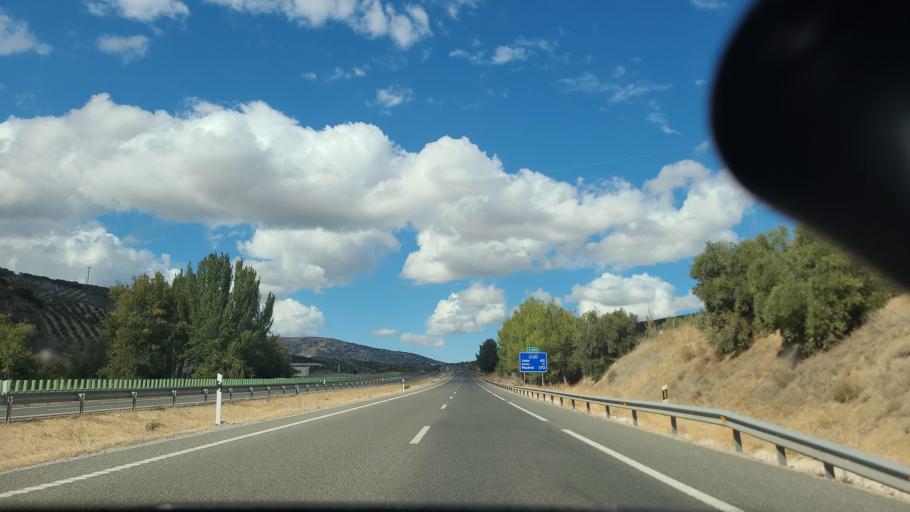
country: ES
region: Andalusia
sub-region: Provincia de Granada
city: Campotejar
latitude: 37.5021
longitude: -3.6287
